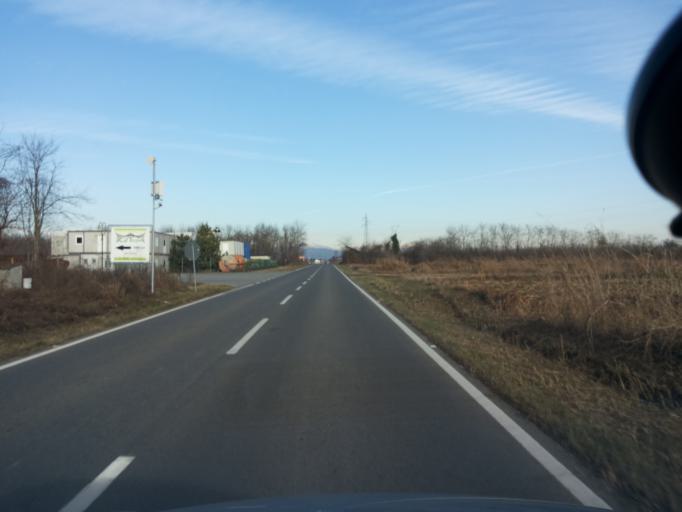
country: IT
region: Piedmont
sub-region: Provincia di Vercelli
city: Ghislarengo
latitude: 45.5394
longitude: 8.3854
